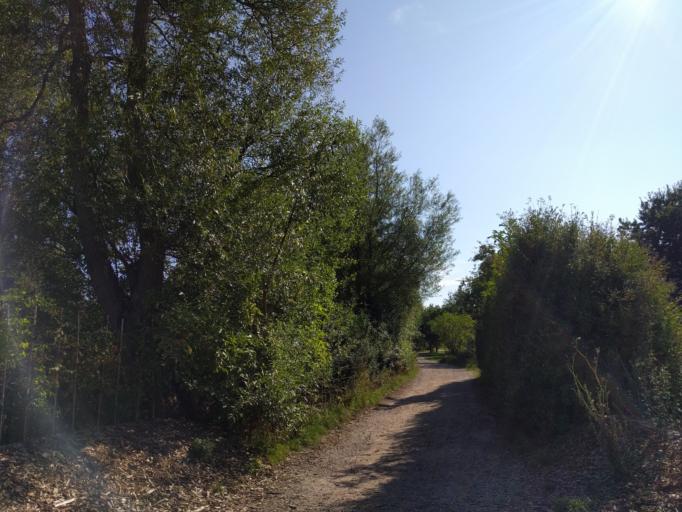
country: DE
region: Schleswig-Holstein
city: Fehmarn
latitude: 54.4058
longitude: 11.1746
